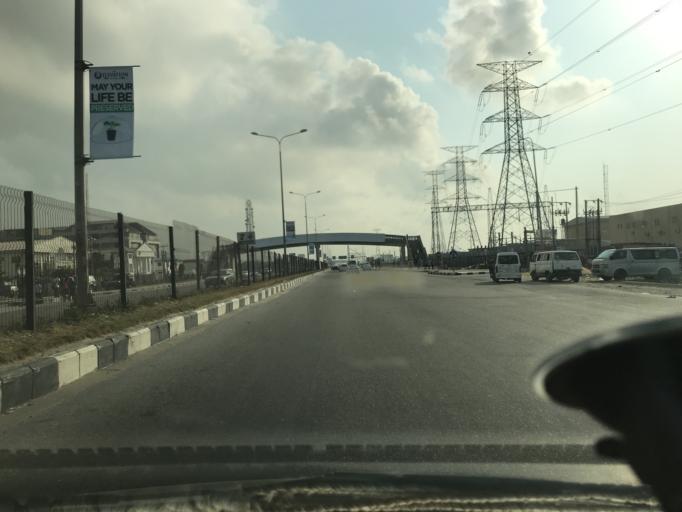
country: NG
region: Lagos
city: Ikoyi
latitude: 6.4358
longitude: 3.5018
